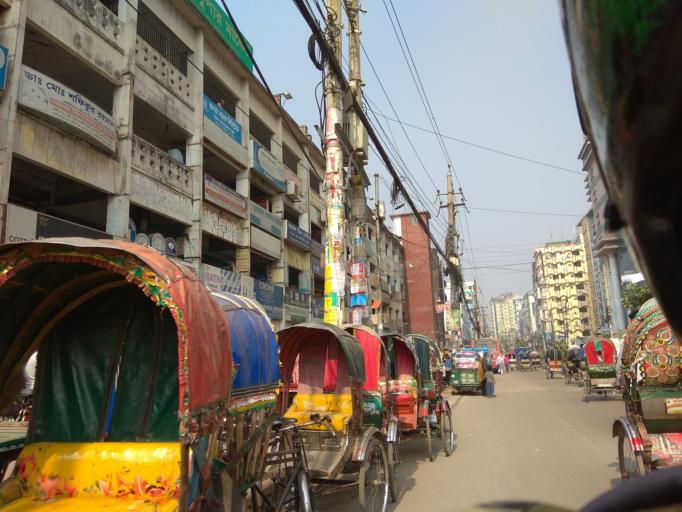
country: BD
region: Dhaka
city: Azimpur
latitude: 23.7541
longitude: 90.3885
